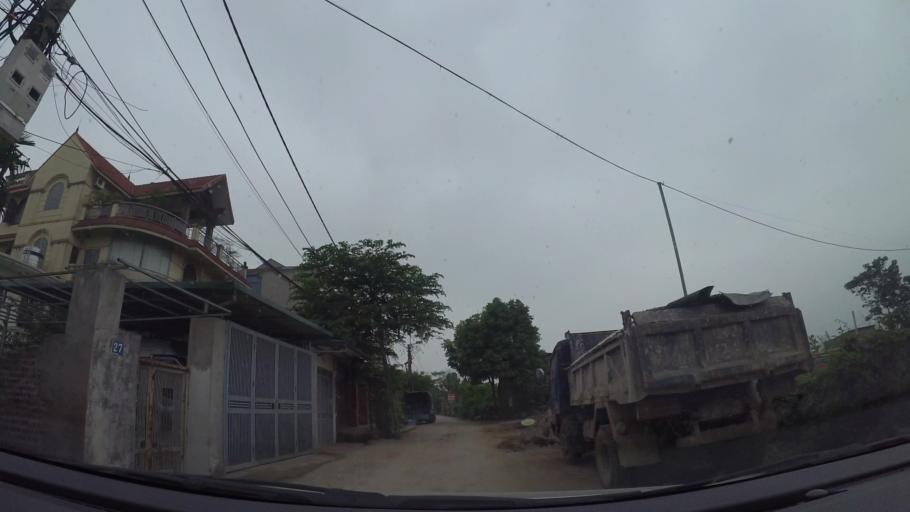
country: VN
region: Ha Noi
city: Tay Ho
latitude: 21.0753
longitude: 105.8275
